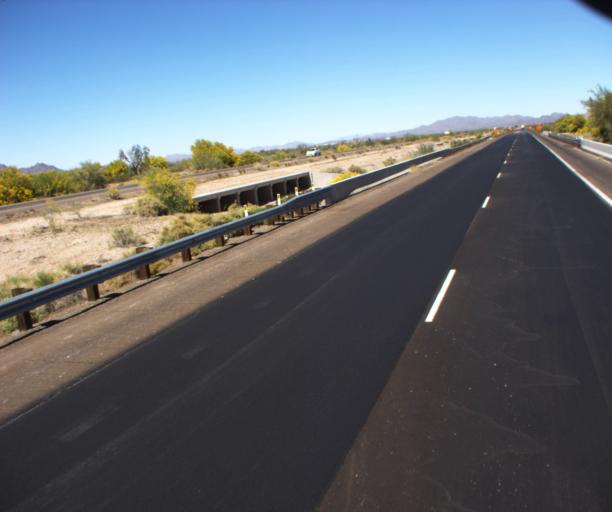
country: US
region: Arizona
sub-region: Maricopa County
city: Gila Bend
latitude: 32.9886
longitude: -112.6645
